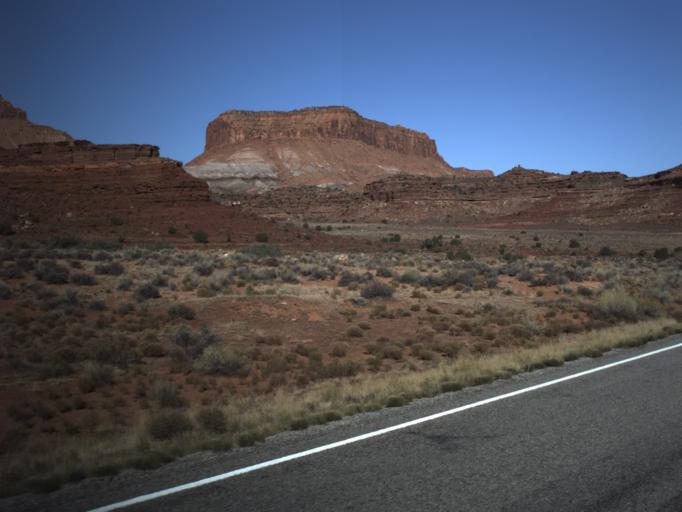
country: US
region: Utah
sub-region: San Juan County
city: Blanding
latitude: 37.7576
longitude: -110.2822
